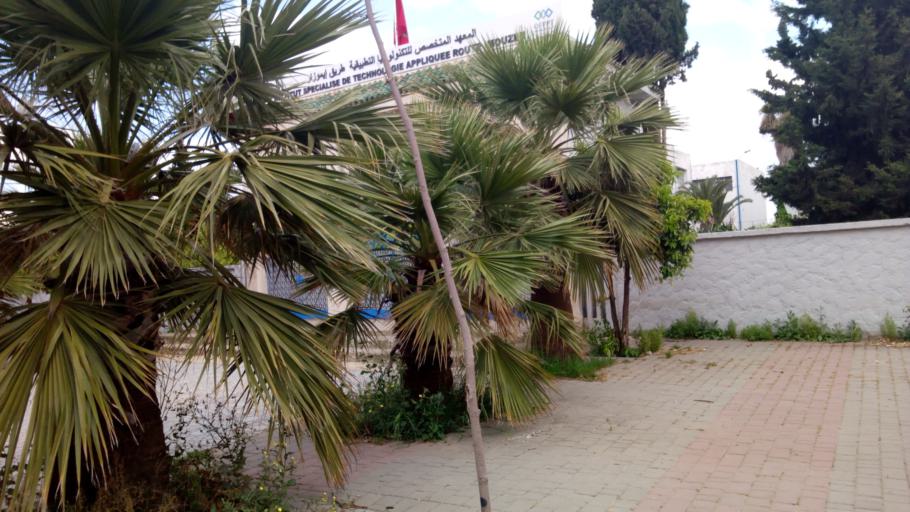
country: MA
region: Fes-Boulemane
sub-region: Fes
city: Fes
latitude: 33.9978
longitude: -4.9911
